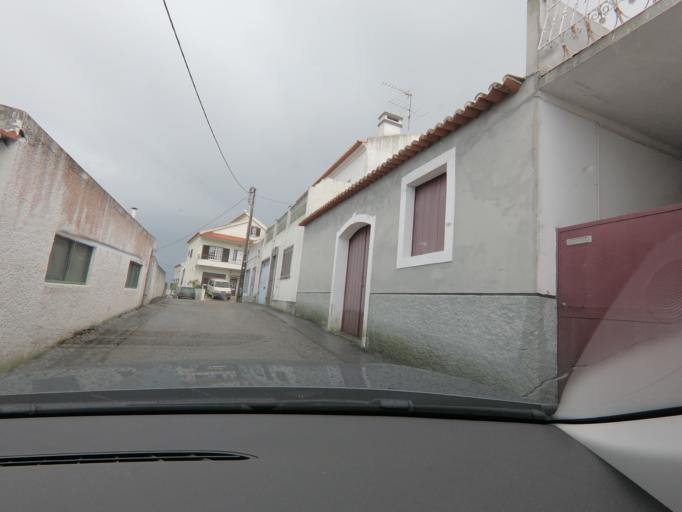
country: PT
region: Lisbon
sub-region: Alenquer
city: Carregado
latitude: 39.0197
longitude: -8.9925
